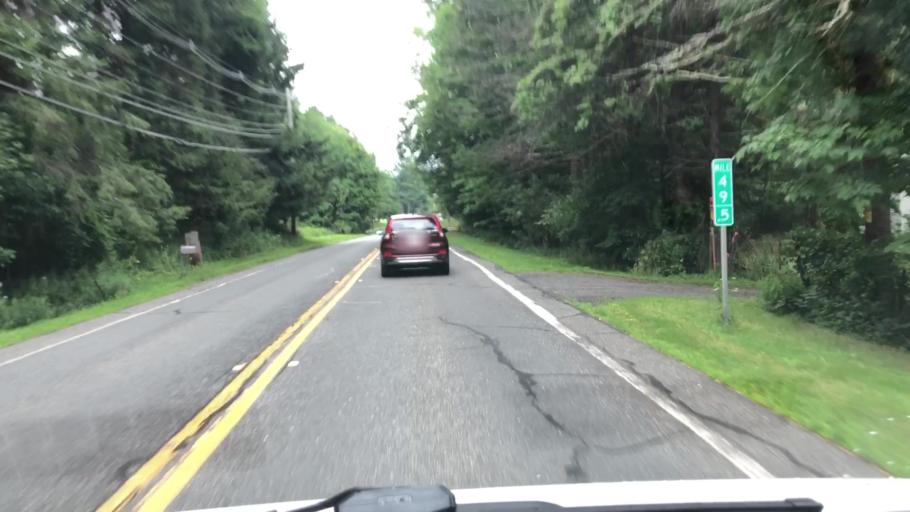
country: US
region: Massachusetts
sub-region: Berkshire County
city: Williamstown
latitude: 42.6918
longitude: -73.2281
